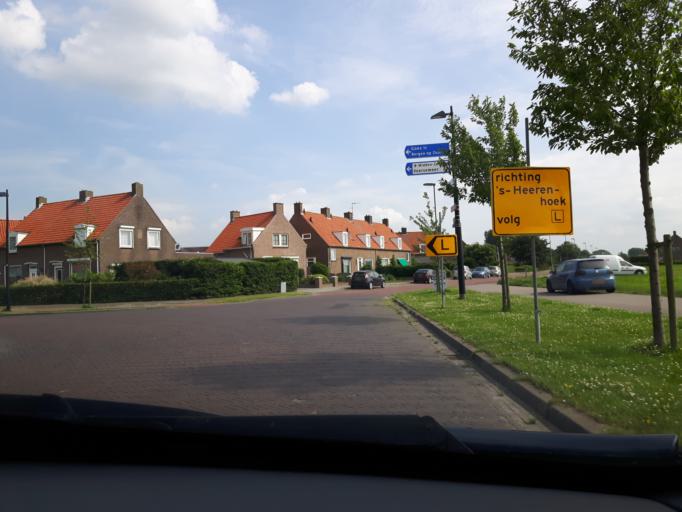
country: NL
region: Zeeland
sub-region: Gemeente Borsele
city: Borssele
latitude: 51.4937
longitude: 3.7480
